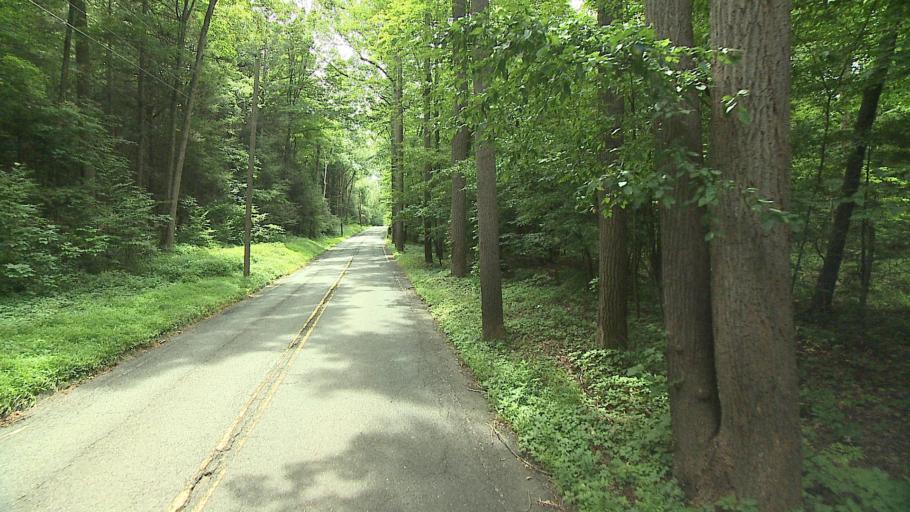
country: US
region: Connecticut
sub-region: Litchfield County
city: New Milford
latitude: 41.5029
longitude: -73.3585
